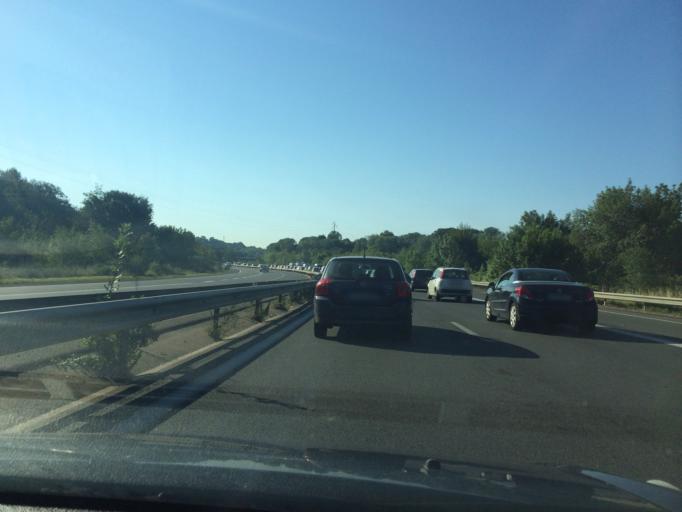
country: FR
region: Languedoc-Roussillon
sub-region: Departement de l'Herault
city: Juvignac
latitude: 43.6088
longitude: 3.8047
